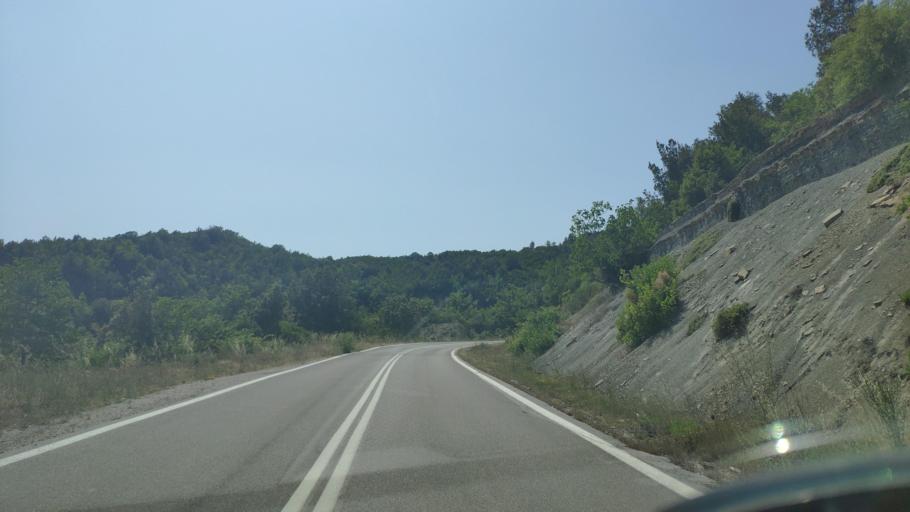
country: GR
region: Epirus
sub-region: Nomos Artas
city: Ano Kalentini
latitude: 39.2197
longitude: 21.1477
